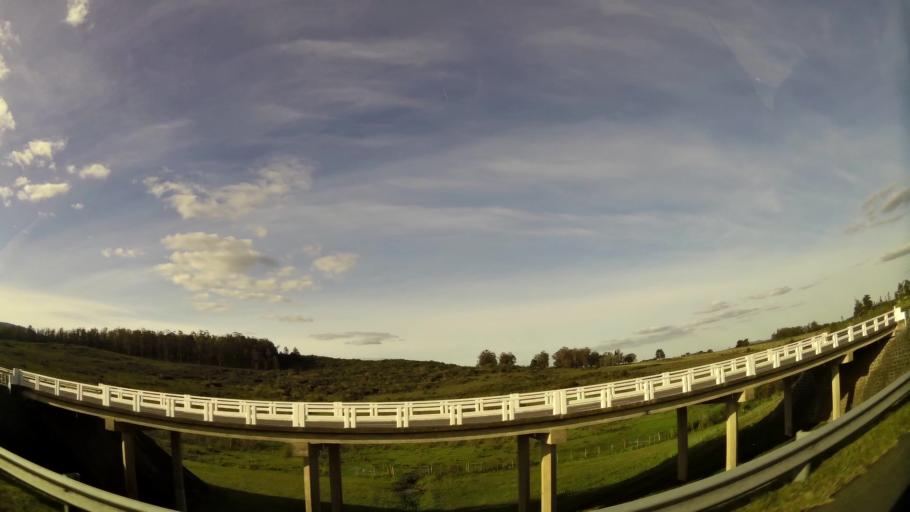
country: UY
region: Maldonado
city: Pan de Azucar
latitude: -34.7856
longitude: -55.2736
